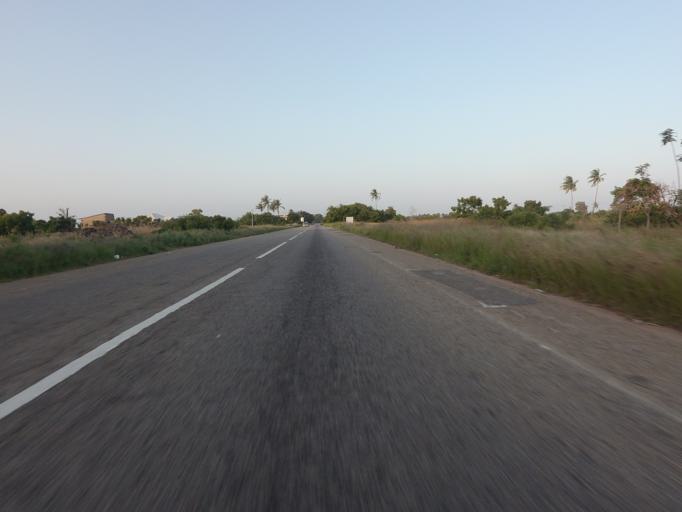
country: GH
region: Volta
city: Anloga
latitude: 5.7868
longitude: 0.8564
